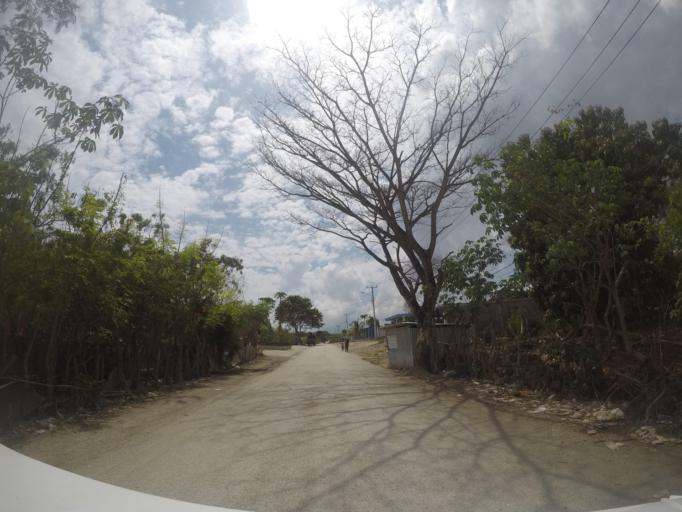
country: TL
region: Baucau
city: Baucau
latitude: -8.4746
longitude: 126.4465
